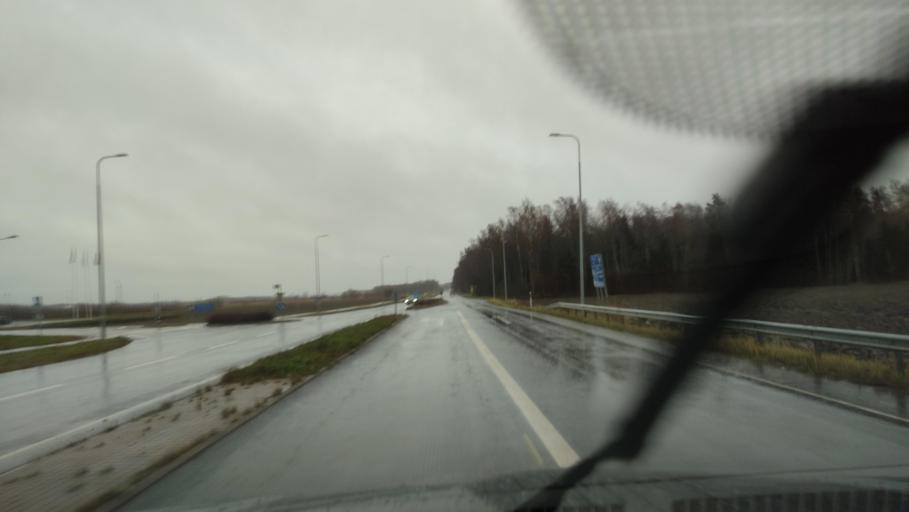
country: FI
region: Ostrobothnia
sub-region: Vaasa
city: Ristinummi
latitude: 63.0486
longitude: 21.7286
